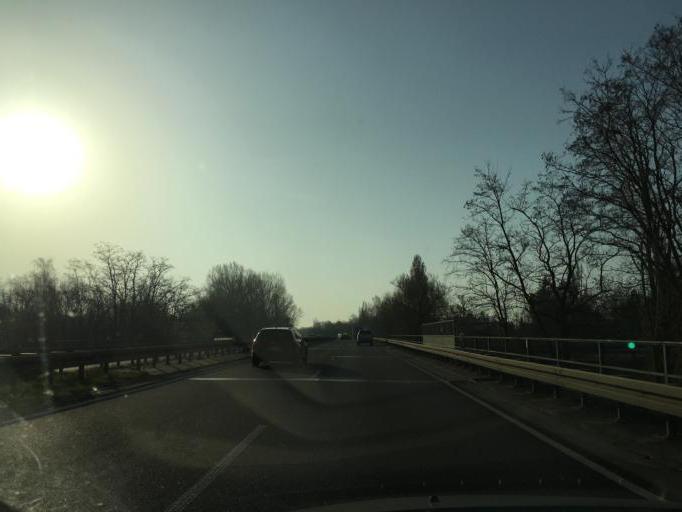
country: DE
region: Saxony
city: Rotha
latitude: 51.2022
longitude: 12.4185
